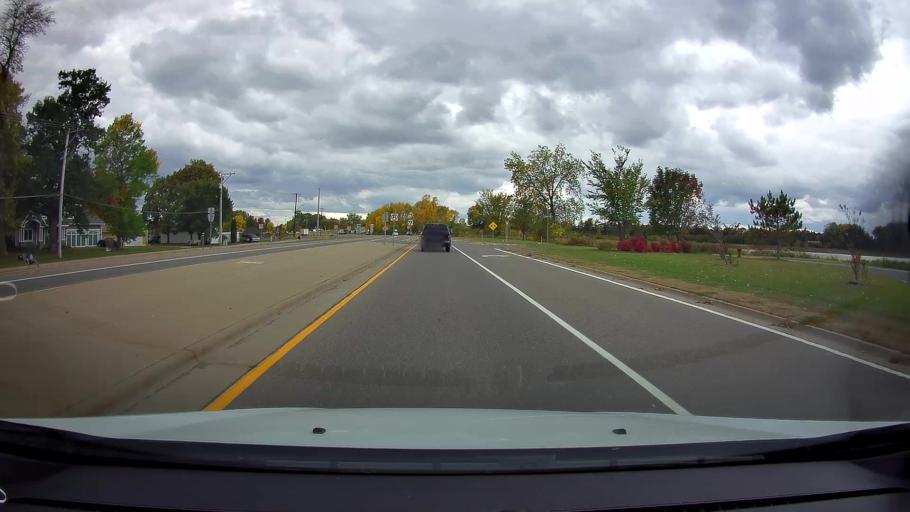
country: US
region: Minnesota
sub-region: Chisago County
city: Chisago City
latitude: 45.3721
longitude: -92.8948
